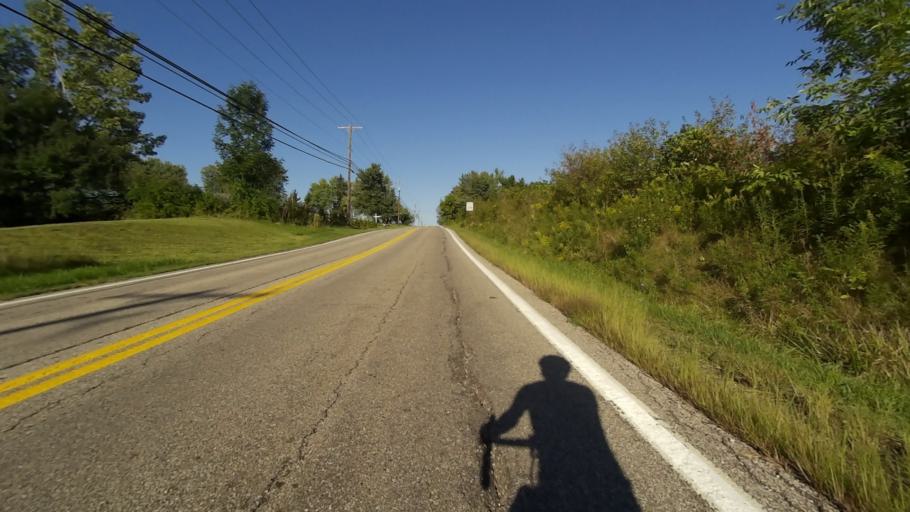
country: US
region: Ohio
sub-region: Portage County
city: Aurora
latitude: 41.2910
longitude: -81.3346
